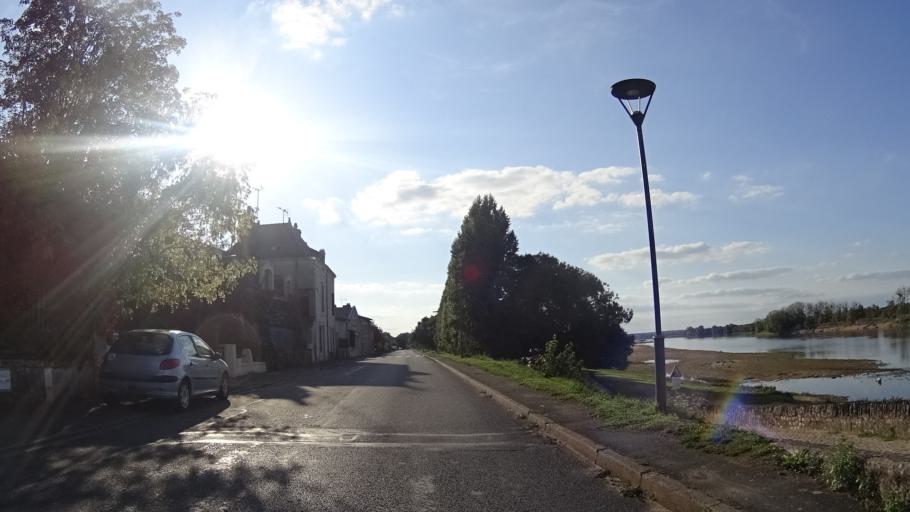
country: FR
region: Pays de la Loire
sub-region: Departement de Maine-et-Loire
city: Montjean-sur-Loire
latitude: 47.3923
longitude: -0.8624
